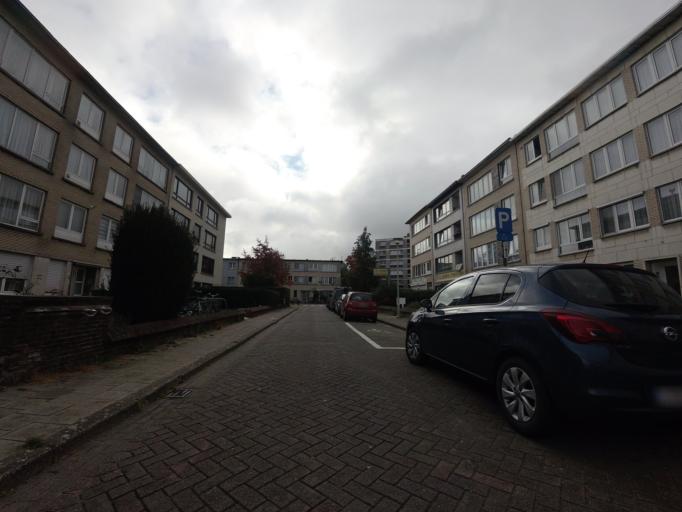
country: BE
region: Flanders
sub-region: Provincie Antwerpen
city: Borsbeek
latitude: 51.2328
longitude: 4.4628
